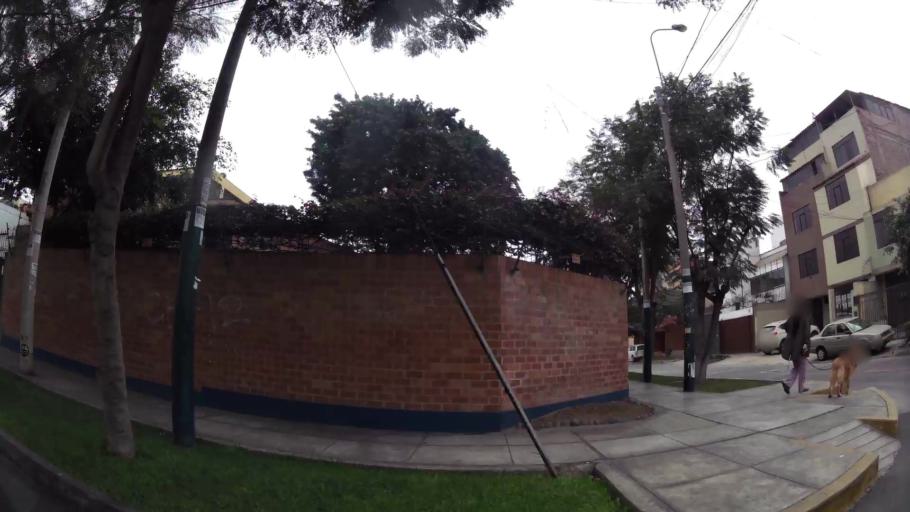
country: PE
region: Lima
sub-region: Lima
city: Surco
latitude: -12.1253
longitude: -76.9984
